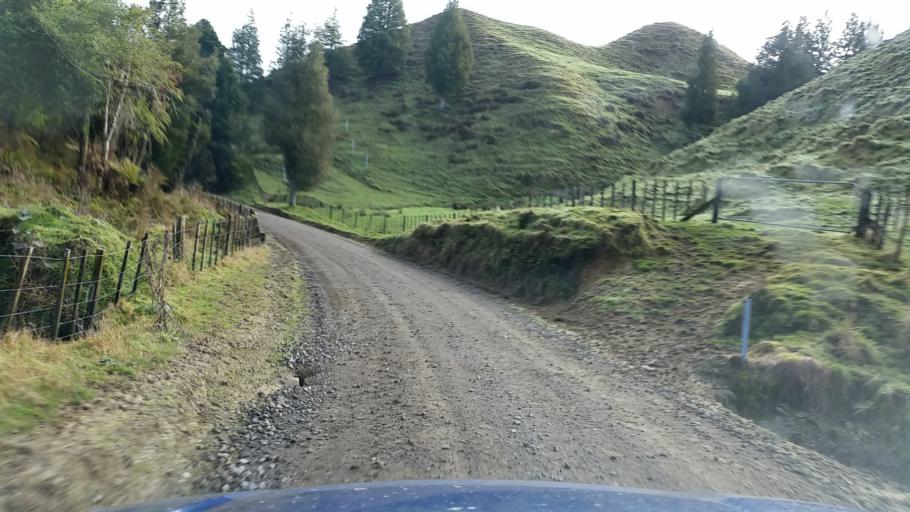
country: NZ
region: Taranaki
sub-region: New Plymouth District
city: Waitara
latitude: -39.1051
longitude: 174.8461
